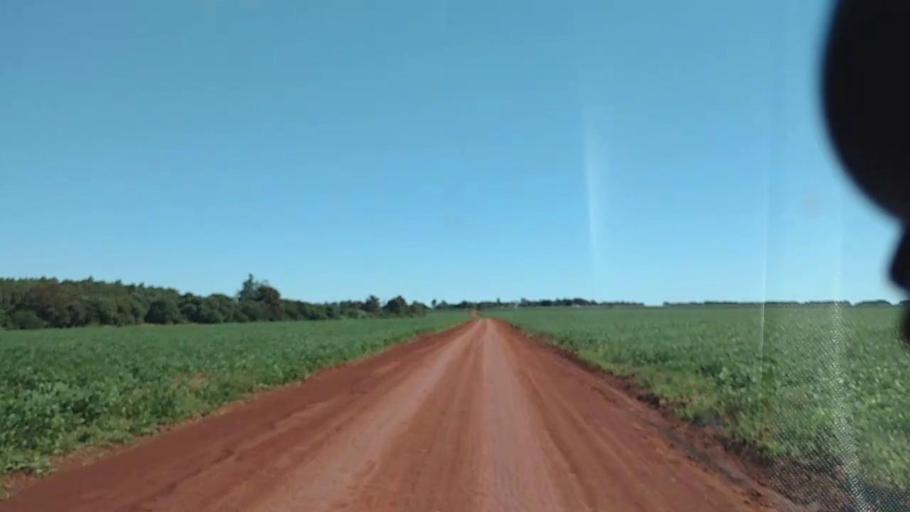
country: PY
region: Alto Parana
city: Naranjal
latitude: -25.9485
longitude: -55.1108
